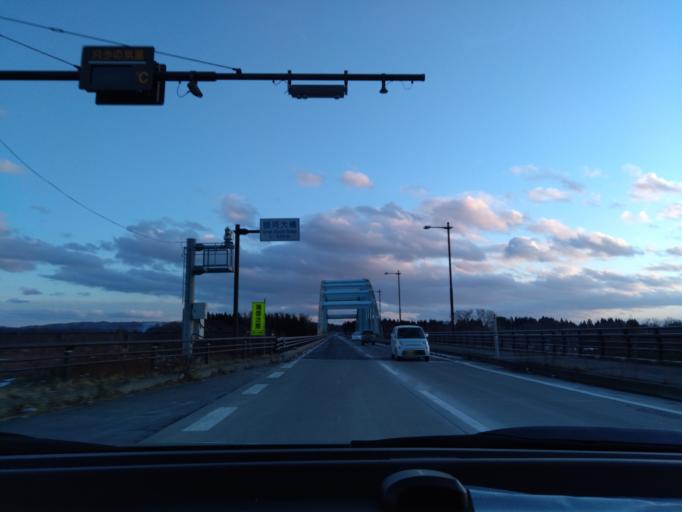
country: JP
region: Iwate
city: Hanamaki
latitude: 39.4026
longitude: 141.1400
